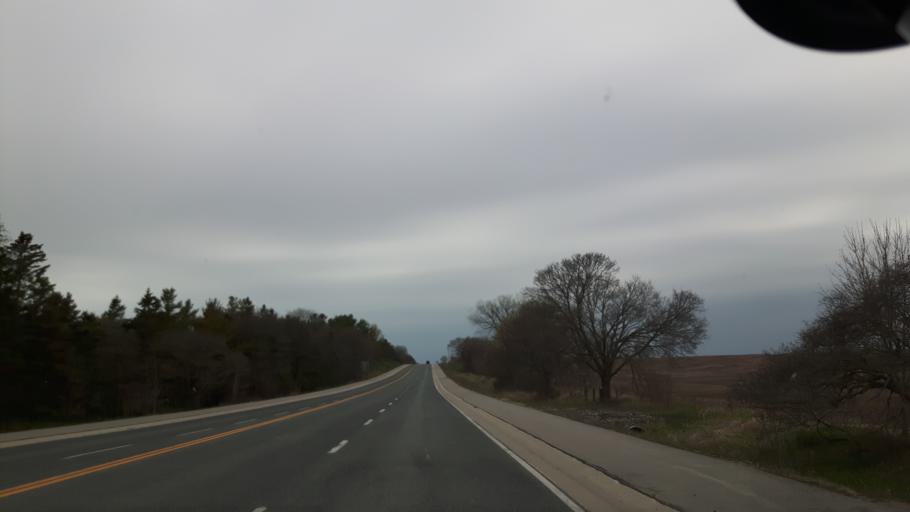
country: CA
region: Ontario
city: Goderich
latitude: 43.6477
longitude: -81.6033
